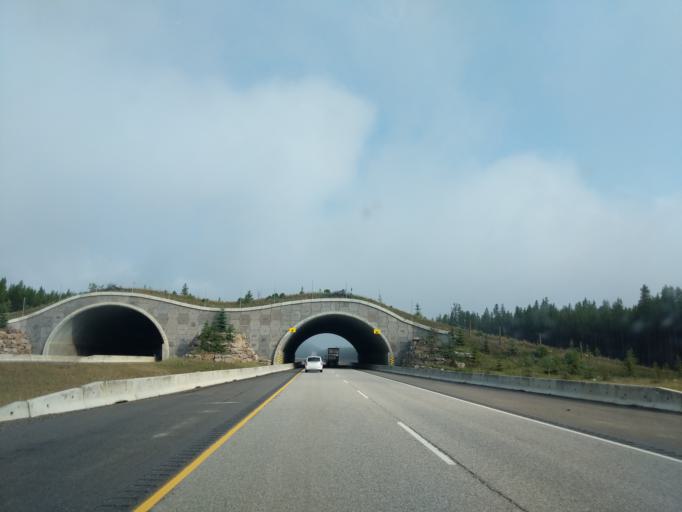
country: CA
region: Alberta
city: Lake Louise
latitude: 51.3001
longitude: -116.0120
